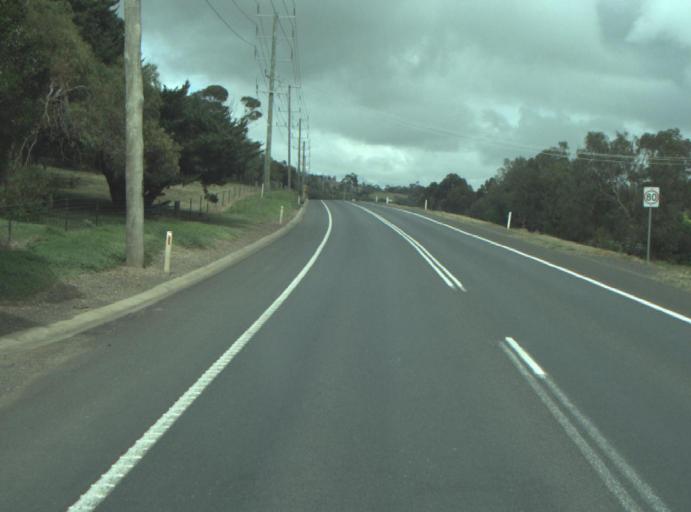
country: AU
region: Victoria
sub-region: Greater Geelong
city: Wandana Heights
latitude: -38.2062
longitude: 144.2890
